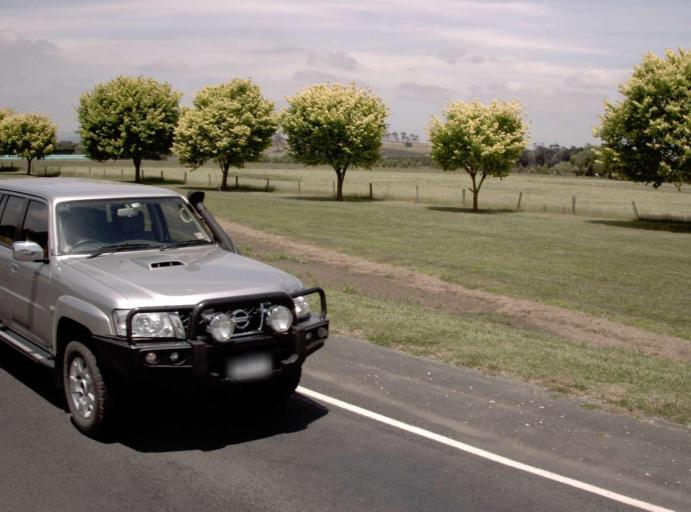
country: AU
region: Victoria
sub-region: Latrobe
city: Traralgon
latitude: -38.2071
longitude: 146.5443
